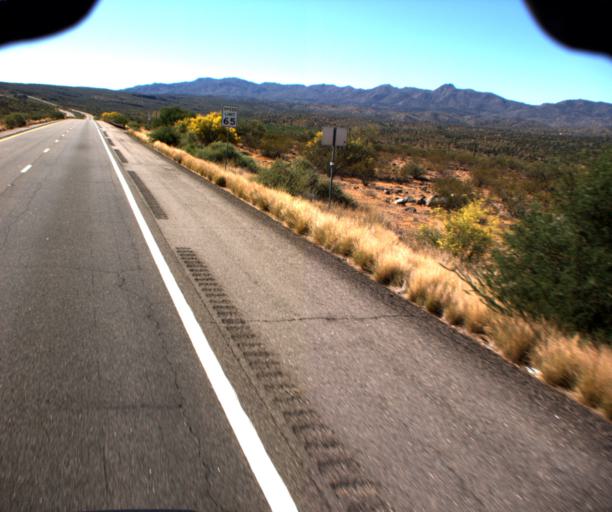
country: US
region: Arizona
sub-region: Yavapai County
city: Bagdad
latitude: 34.5191
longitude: -113.4223
